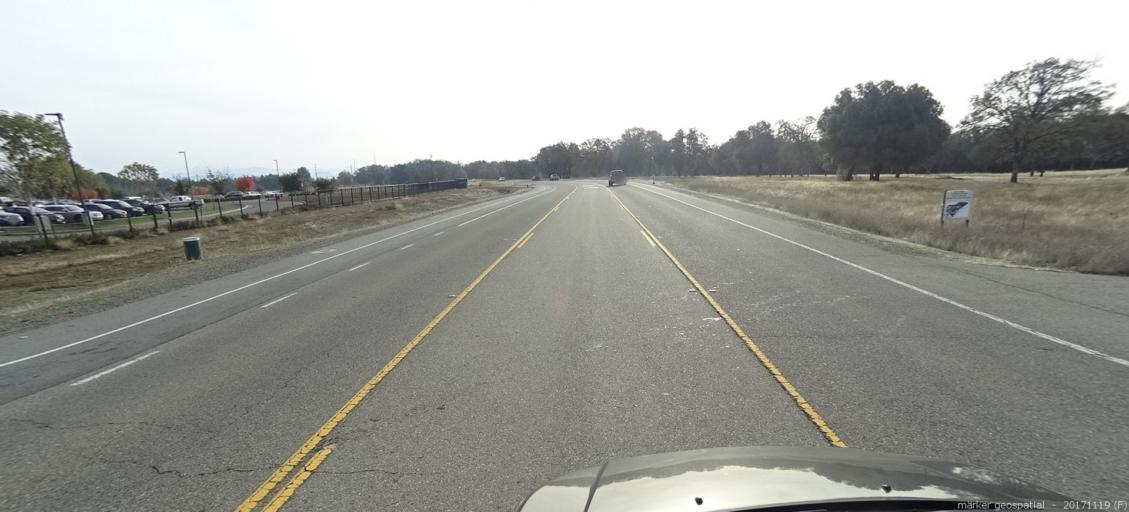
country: US
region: California
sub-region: Shasta County
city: Anderson
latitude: 40.5068
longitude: -122.3121
